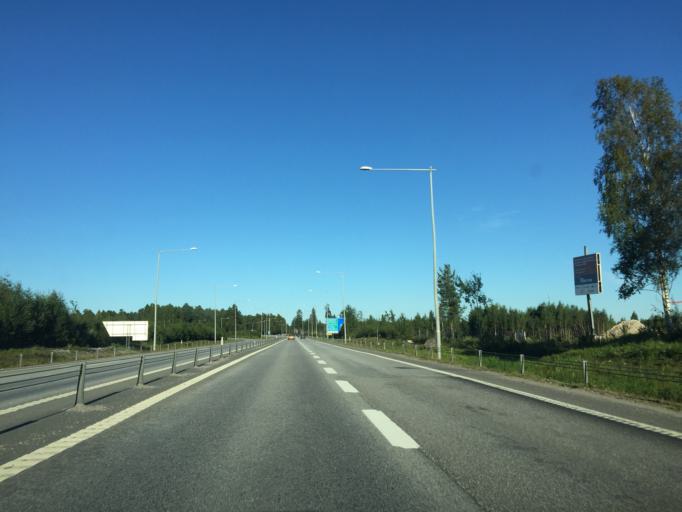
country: SE
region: OErebro
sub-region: Orebro Kommun
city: Orebro
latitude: 59.2395
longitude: 15.1240
